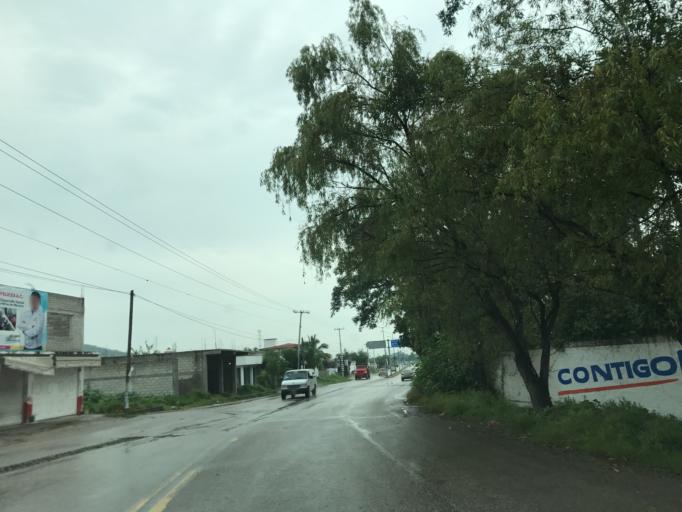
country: MX
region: Morelos
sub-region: Ayala
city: Ciudad Ayala
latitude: 18.7547
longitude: -98.9850
